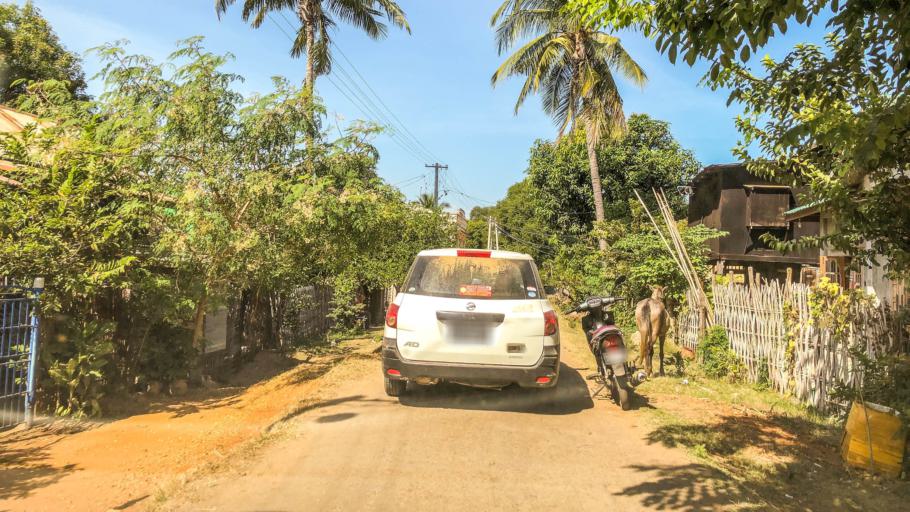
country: MM
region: Magway
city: Magway
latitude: 19.9735
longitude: 95.0395
